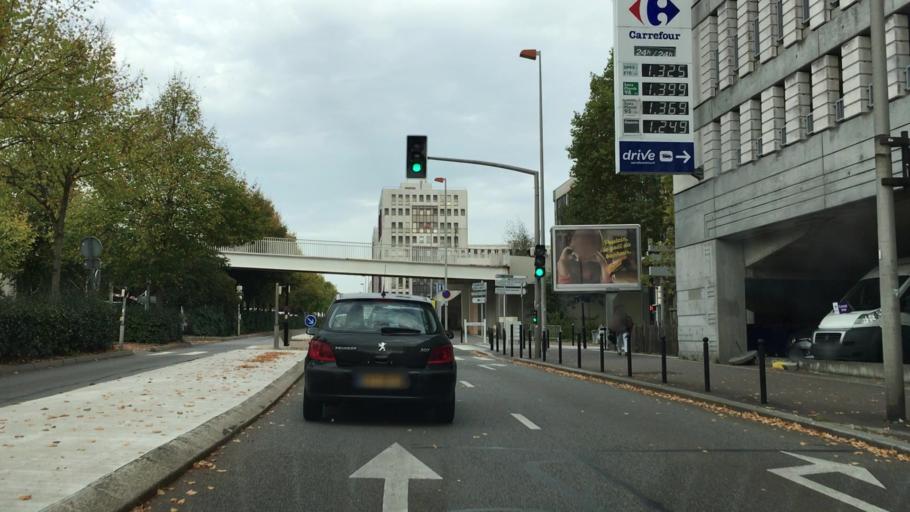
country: FR
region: Ile-de-France
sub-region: Departement des Yvelines
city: Montigny-le-Bretonneux
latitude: 48.7861
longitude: 2.0431
